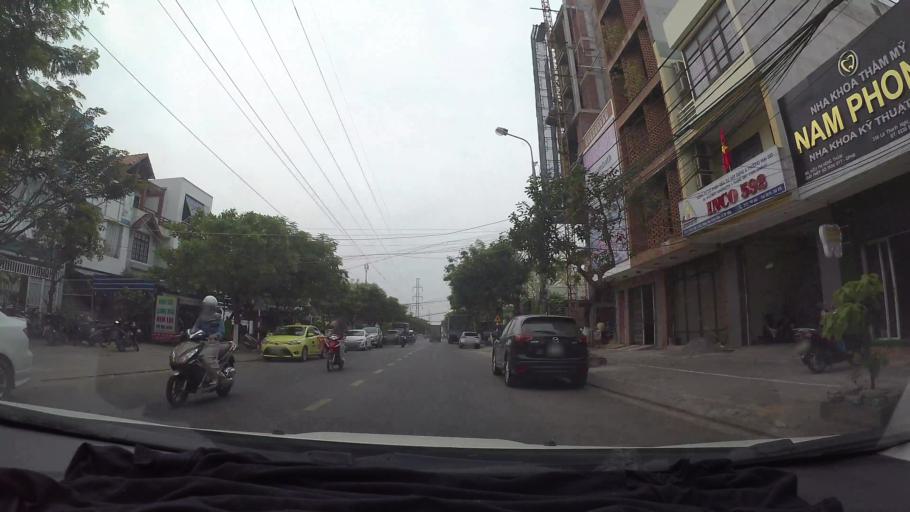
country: VN
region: Da Nang
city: Cam Le
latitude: 16.0353
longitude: 108.2184
